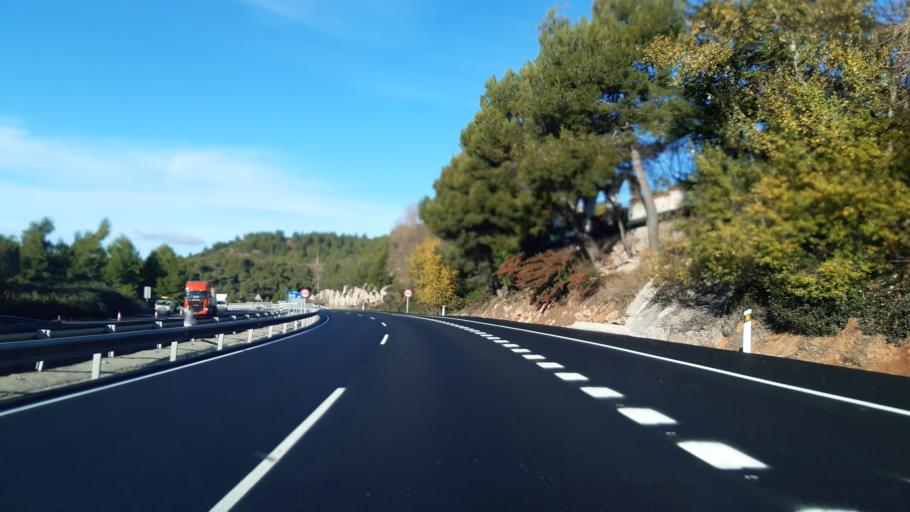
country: ES
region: Catalonia
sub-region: Provincia de Barcelona
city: Collbato
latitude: 41.5941
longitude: 1.7670
